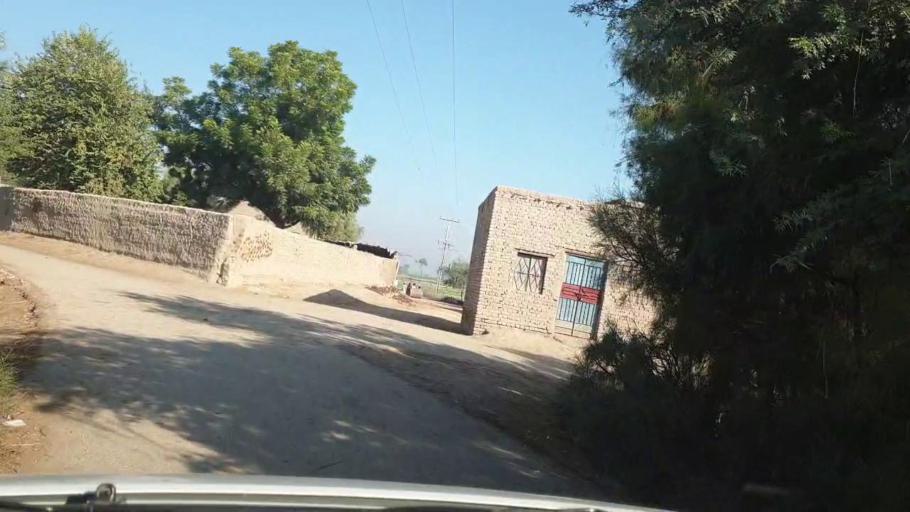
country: PK
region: Sindh
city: Dadu
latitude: 26.6741
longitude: 67.8390
